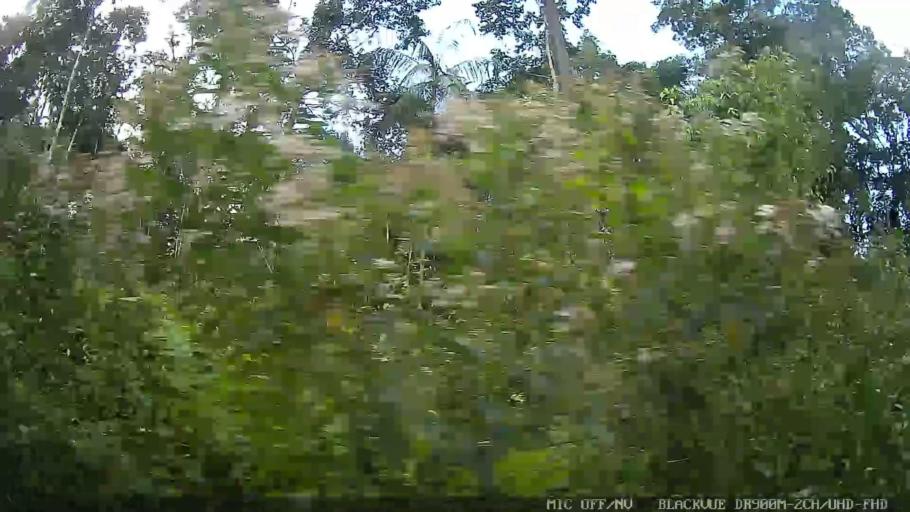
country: BR
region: Sao Paulo
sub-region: Peruibe
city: Peruibe
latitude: -24.1823
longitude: -46.9392
